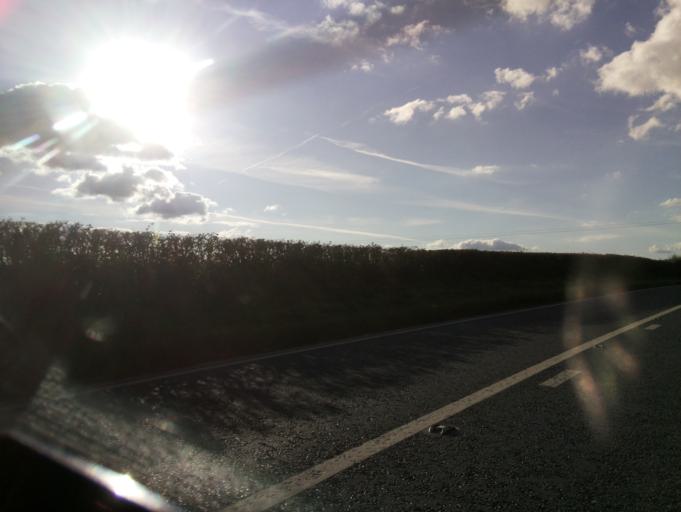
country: GB
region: England
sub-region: Herefordshire
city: Bridge Sollers
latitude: 52.0750
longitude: -2.8383
